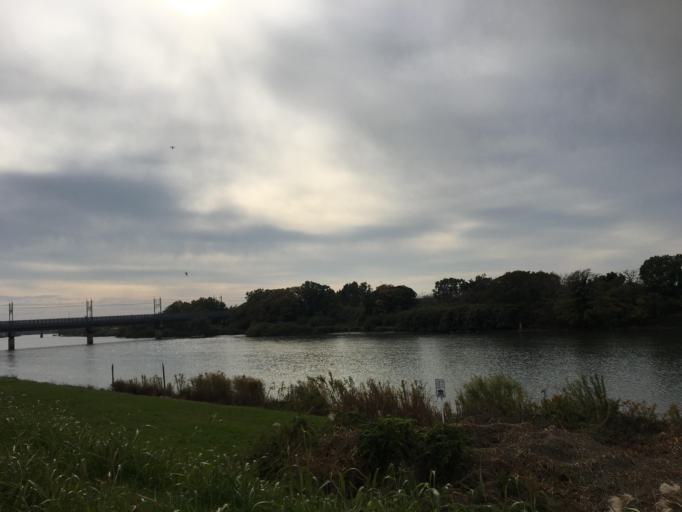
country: JP
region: Saitama
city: Yoshikawa
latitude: 35.8794
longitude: 139.8406
